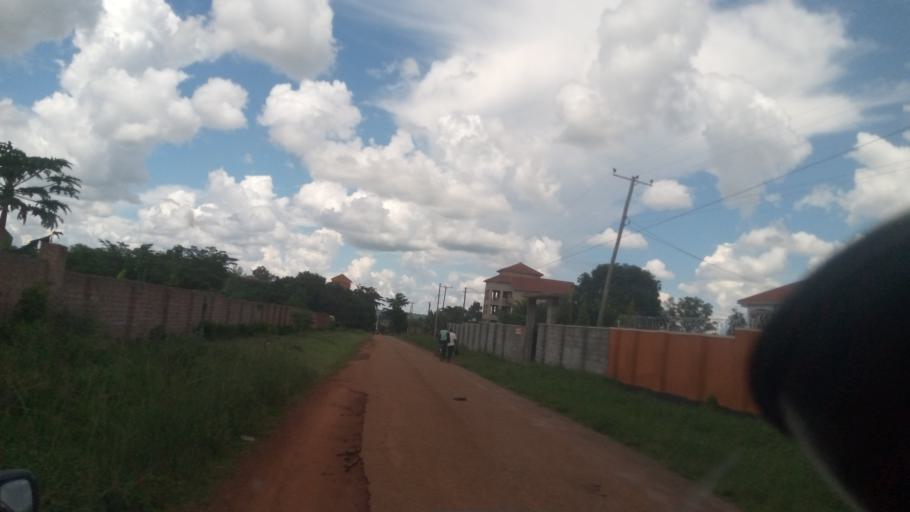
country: UG
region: Northern Region
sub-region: Lira District
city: Lira
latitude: 2.2405
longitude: 32.9053
